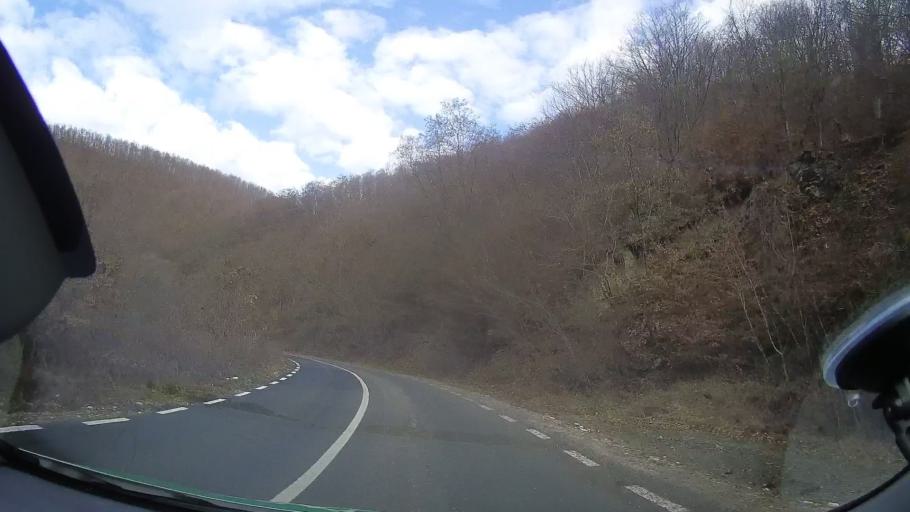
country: RO
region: Cluj
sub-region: Comuna Baisoara
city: Baisoara
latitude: 46.5868
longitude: 23.4482
